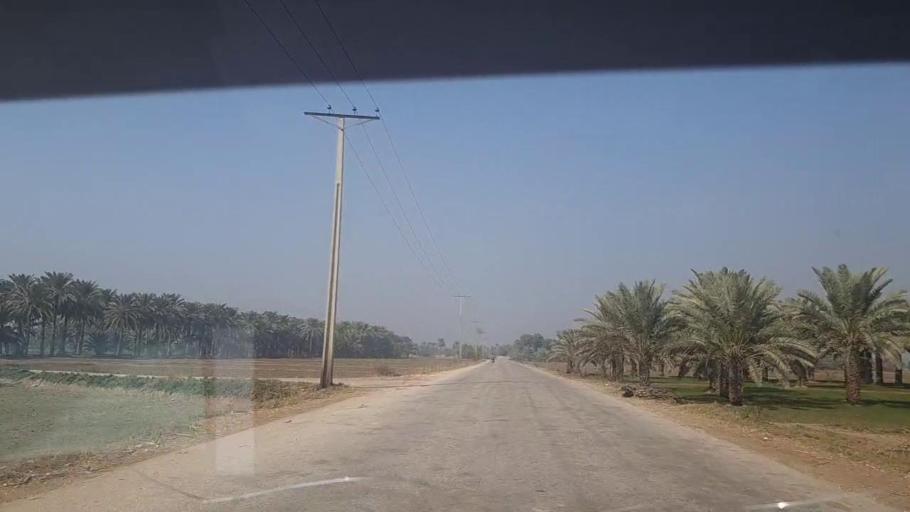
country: PK
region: Sindh
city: Kot Diji
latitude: 27.3672
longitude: 68.7022
